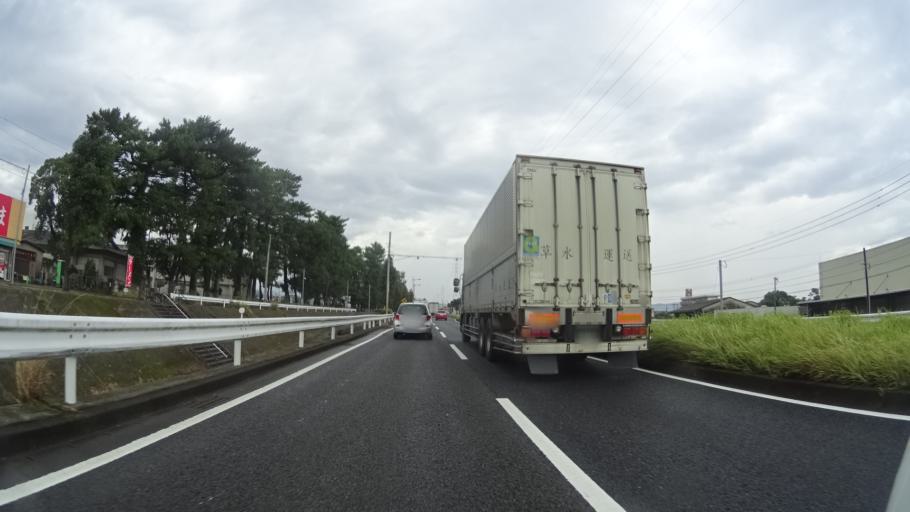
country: JP
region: Kagoshima
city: Kajiki
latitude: 31.7121
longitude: 130.6167
